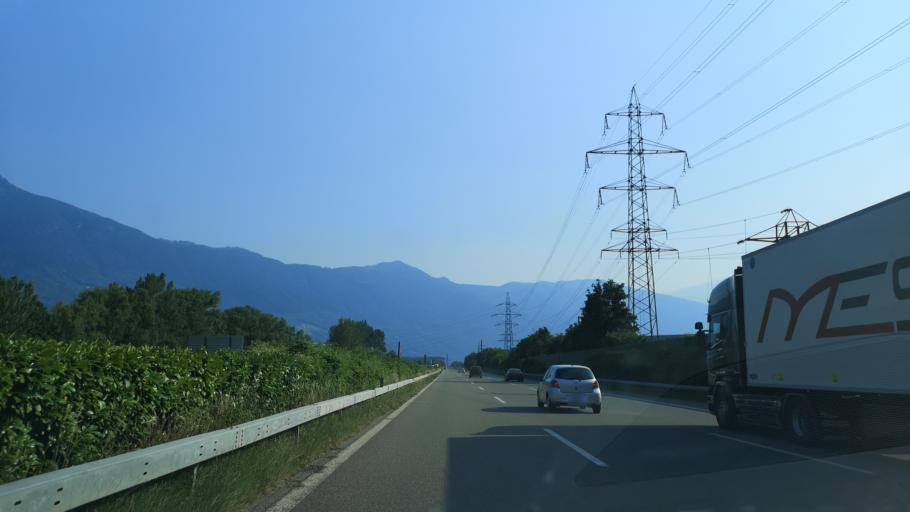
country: CH
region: Ticino
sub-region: Bellinzona District
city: Monte Carasso
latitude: 46.1898
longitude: 9.0061
